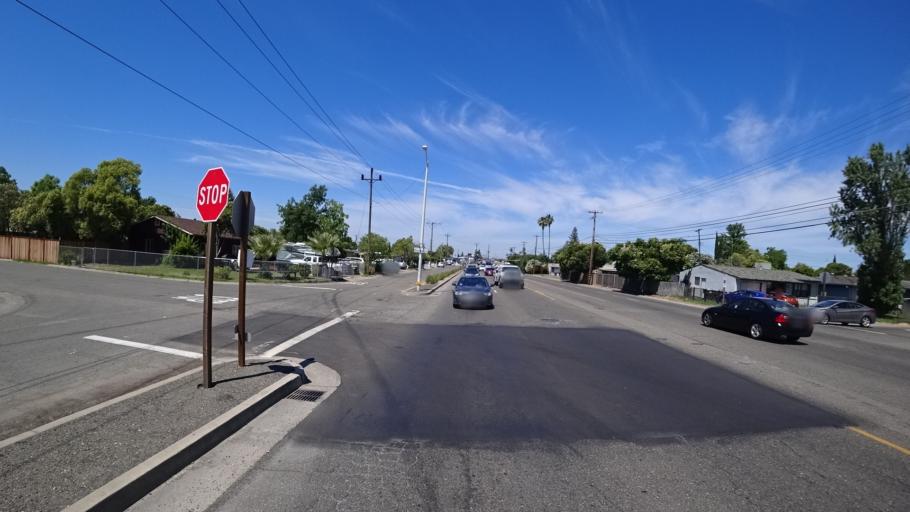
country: US
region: California
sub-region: Sacramento County
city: Arden-Arcade
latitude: 38.6108
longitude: -121.4175
